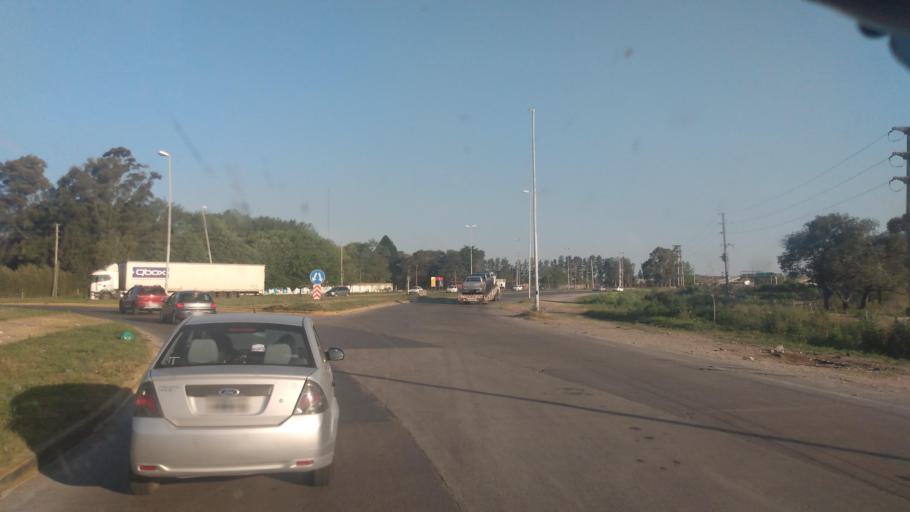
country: AR
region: Buenos Aires
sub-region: Partido de Campana
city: Campana
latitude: -34.2031
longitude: -58.9602
